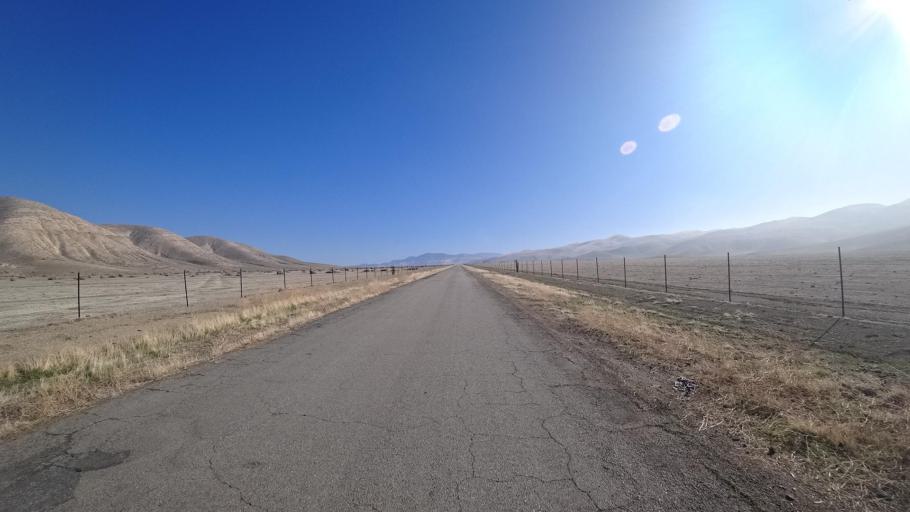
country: US
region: California
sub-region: Kern County
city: Maricopa
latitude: 35.0028
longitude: -119.4056
